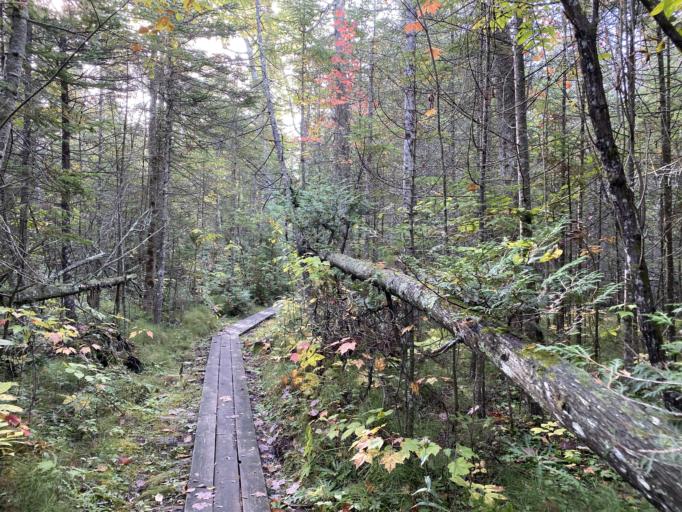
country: US
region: Michigan
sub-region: Mackinac County
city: Saint Ignace
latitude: 45.7411
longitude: -84.8900
